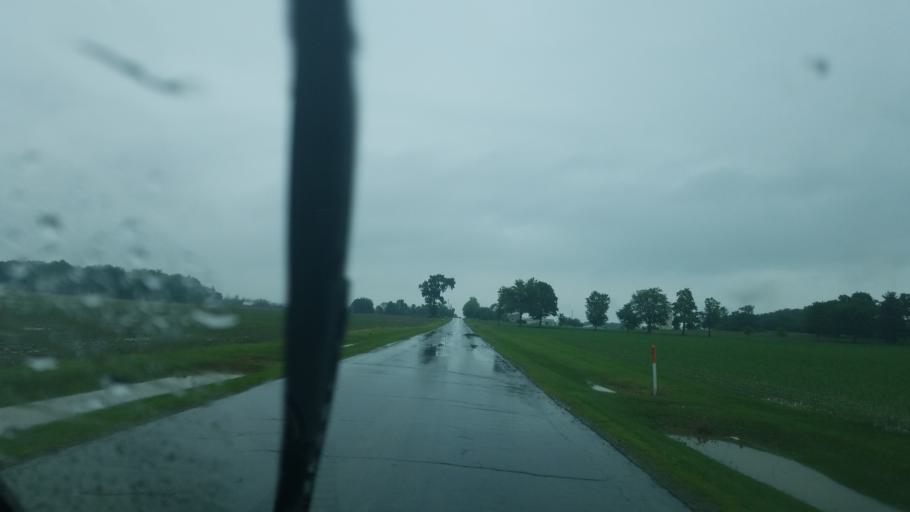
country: US
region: Ohio
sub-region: Huron County
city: Plymouth
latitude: 40.9844
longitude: -82.6056
